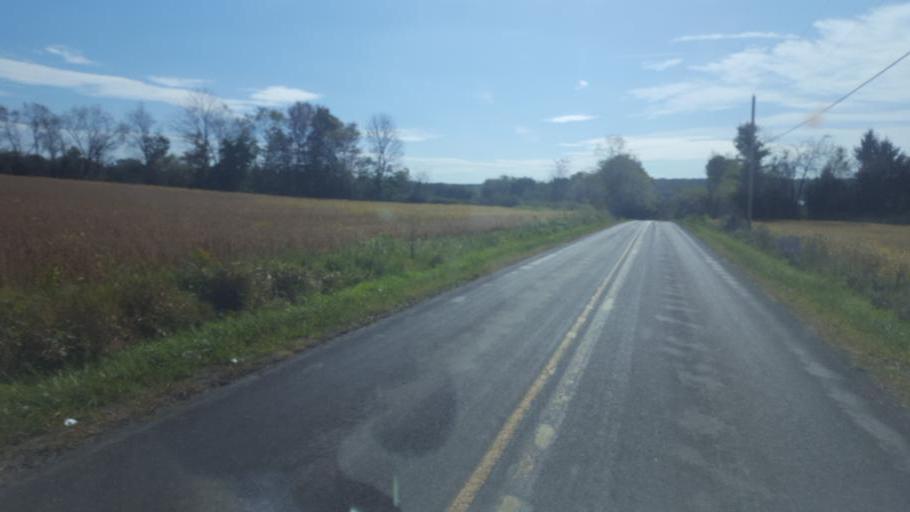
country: US
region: Pennsylvania
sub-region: Mercer County
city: Greenville
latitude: 41.4102
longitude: -80.4523
